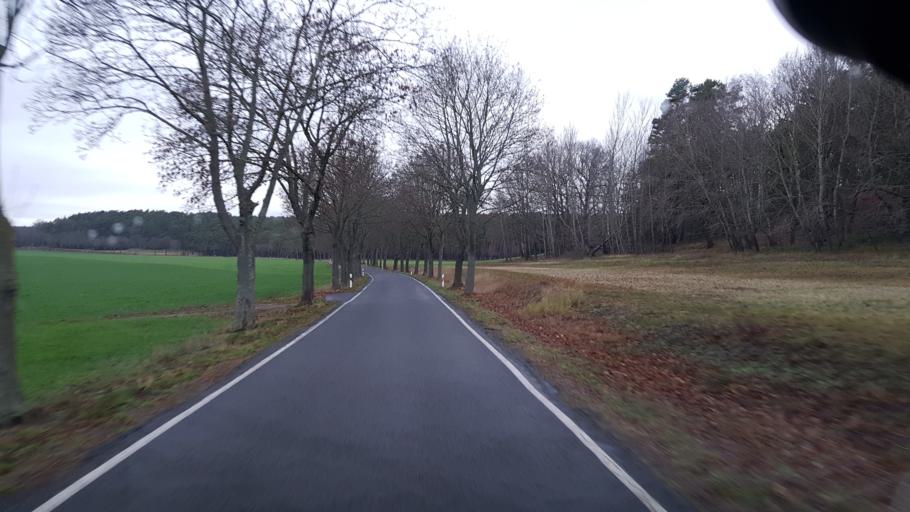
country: DE
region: Brandenburg
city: Hohenbucko
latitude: 51.7398
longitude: 13.4552
